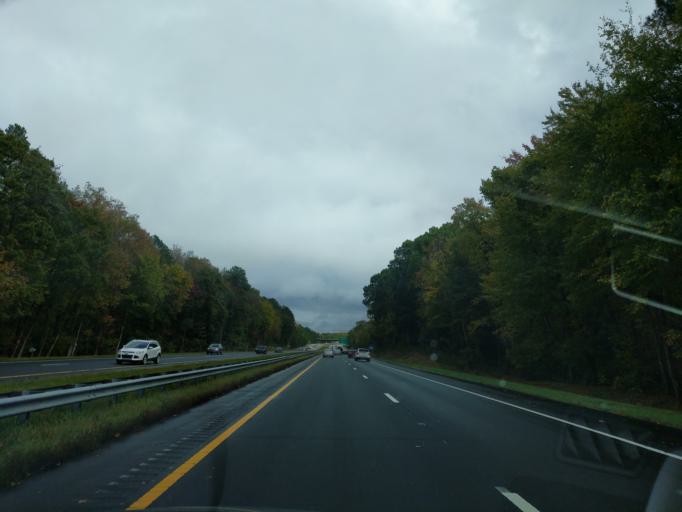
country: US
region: North Carolina
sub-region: Durham County
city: Durham
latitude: 36.0380
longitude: -78.9907
